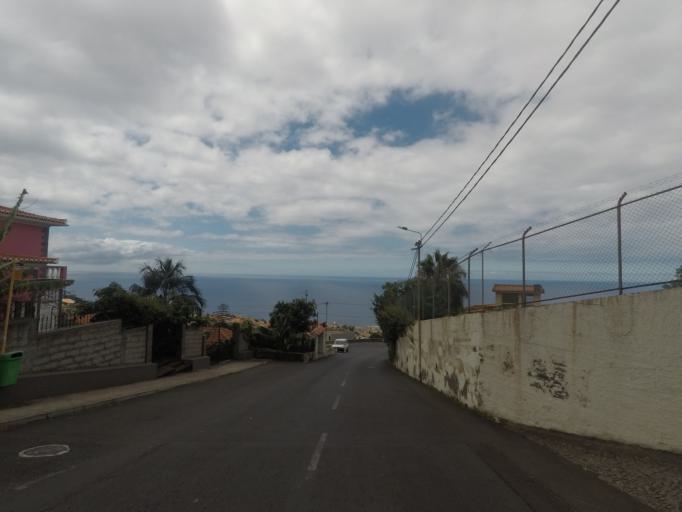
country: PT
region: Madeira
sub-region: Funchal
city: Nossa Senhora do Monte
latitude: 32.6607
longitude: -16.8956
